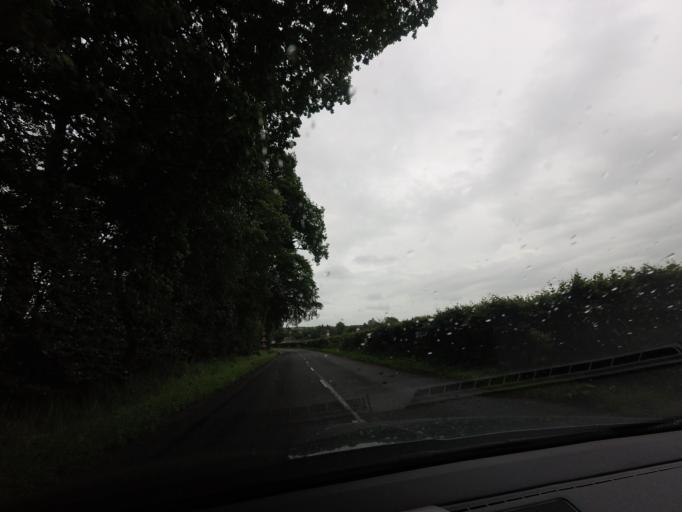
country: GB
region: Scotland
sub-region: Aberdeenshire
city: Turriff
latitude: 57.5412
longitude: -2.4826
